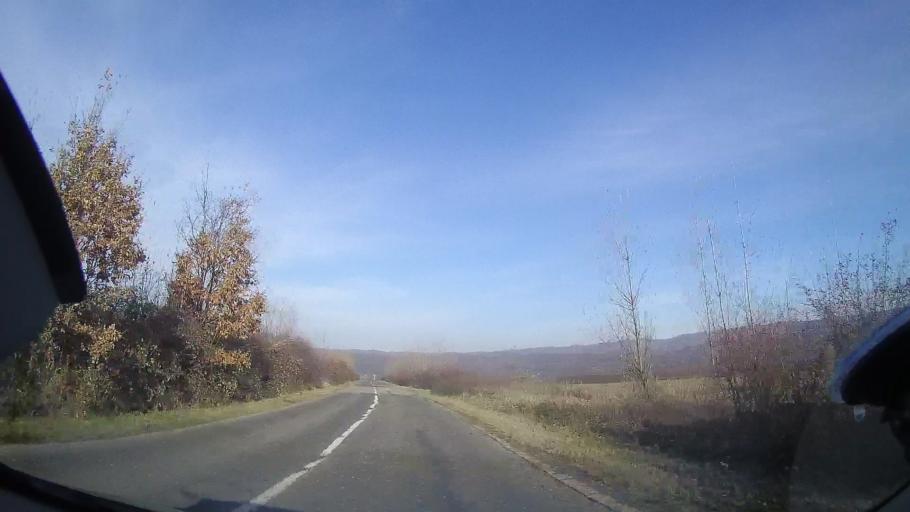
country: RO
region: Bihor
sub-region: Comuna Brusturi
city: Brusturi
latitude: 47.1180
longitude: 22.2674
